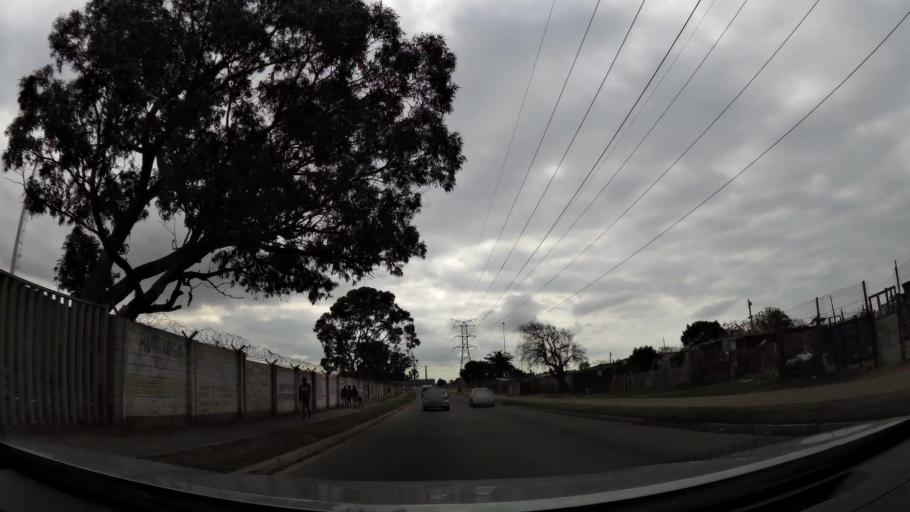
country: ZA
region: Eastern Cape
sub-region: Nelson Mandela Bay Metropolitan Municipality
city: Port Elizabeth
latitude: -33.8840
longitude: 25.5963
